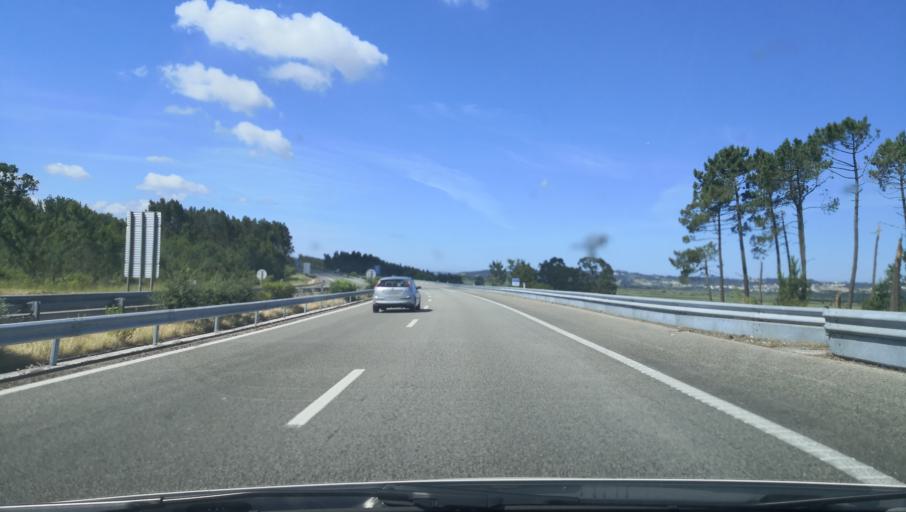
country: PT
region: Coimbra
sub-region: Montemor-O-Velho
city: Montemor-o-Velho
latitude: 40.1896
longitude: -8.6987
